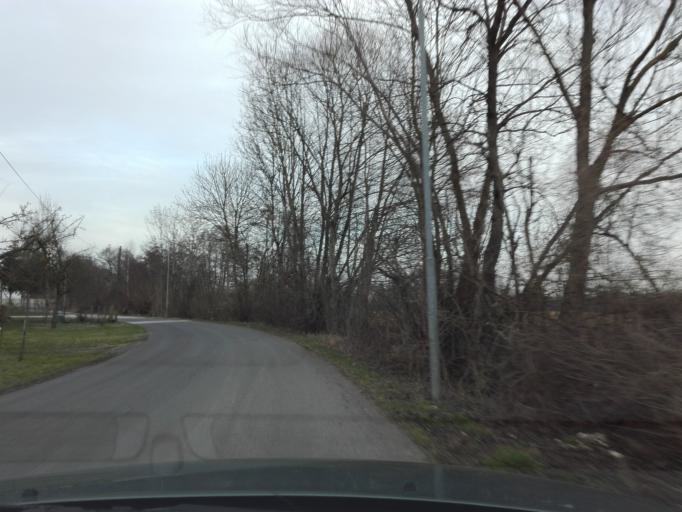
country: AT
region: Upper Austria
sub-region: Politischer Bezirk Linz-Land
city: Horsching
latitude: 48.1998
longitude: 14.1646
